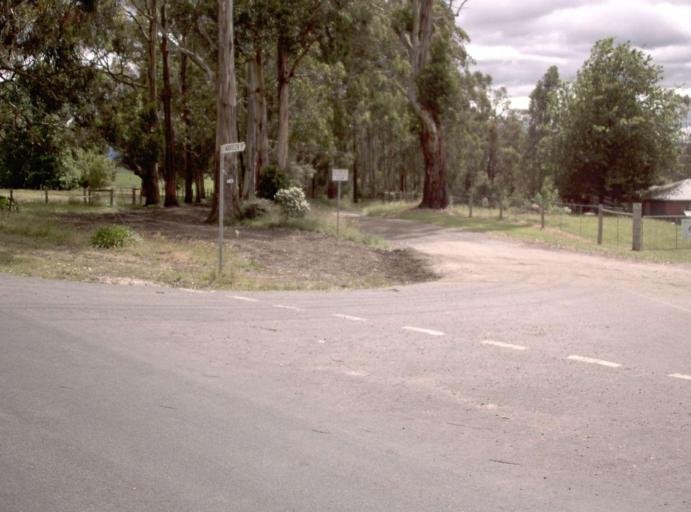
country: AU
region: Victoria
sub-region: Latrobe
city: Moe
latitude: -38.0303
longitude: 146.1655
